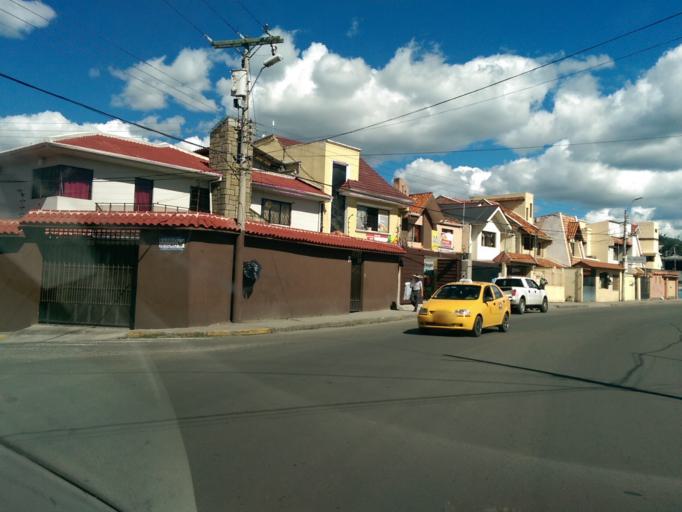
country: EC
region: Azuay
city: Cuenca
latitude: -2.9043
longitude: -79.0193
